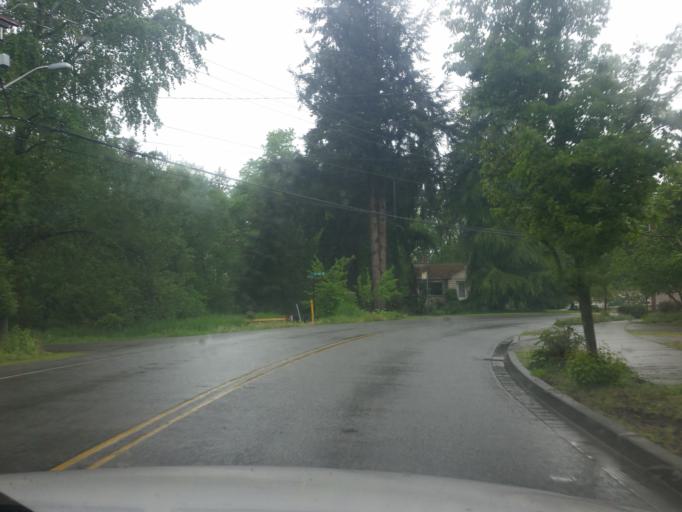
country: US
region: Washington
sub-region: King County
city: Kenmore
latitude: 47.7398
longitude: -122.2368
